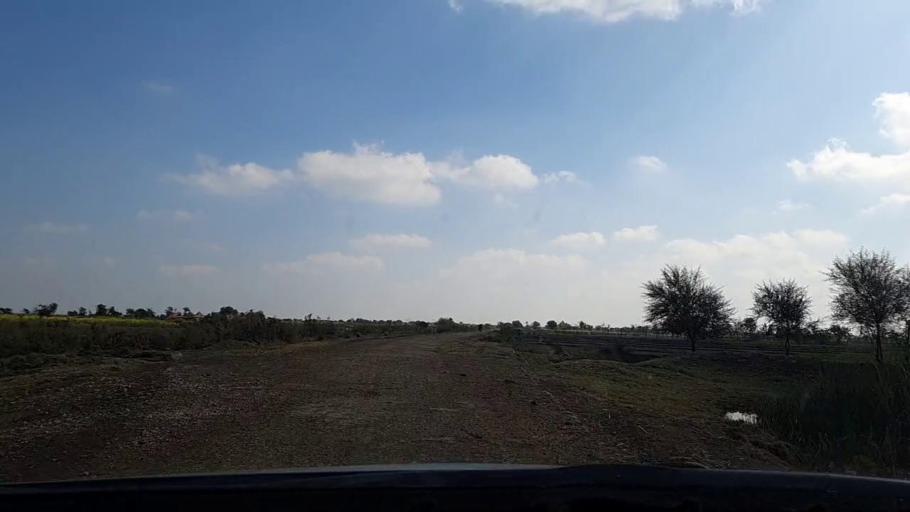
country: PK
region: Sindh
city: Pithoro
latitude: 25.7299
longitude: 69.2865
